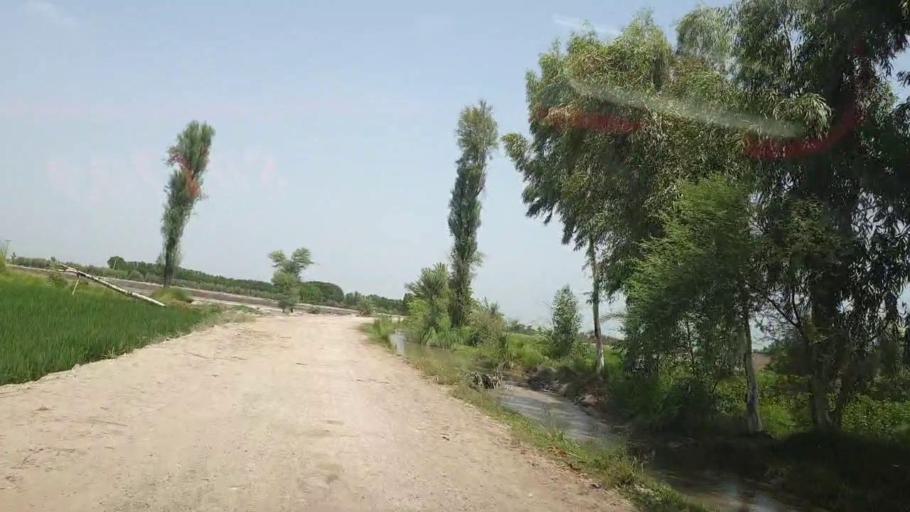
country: PK
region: Sindh
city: Daulatpur
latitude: 26.4882
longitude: 68.1389
